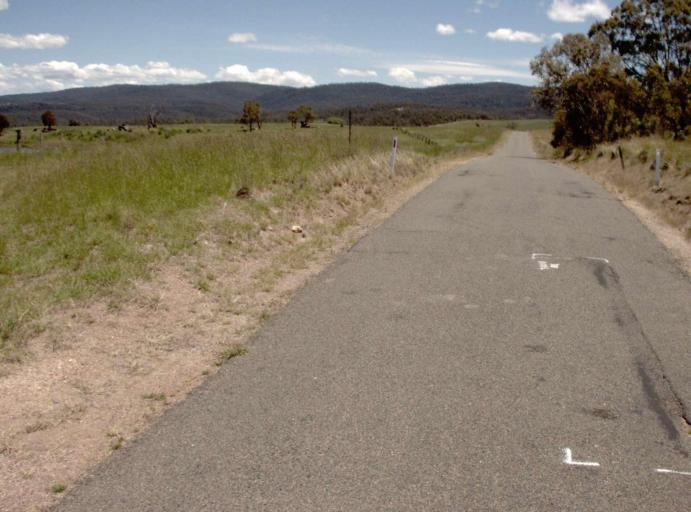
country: AU
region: New South Wales
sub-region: Snowy River
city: Jindabyne
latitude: -37.0947
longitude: 148.2639
